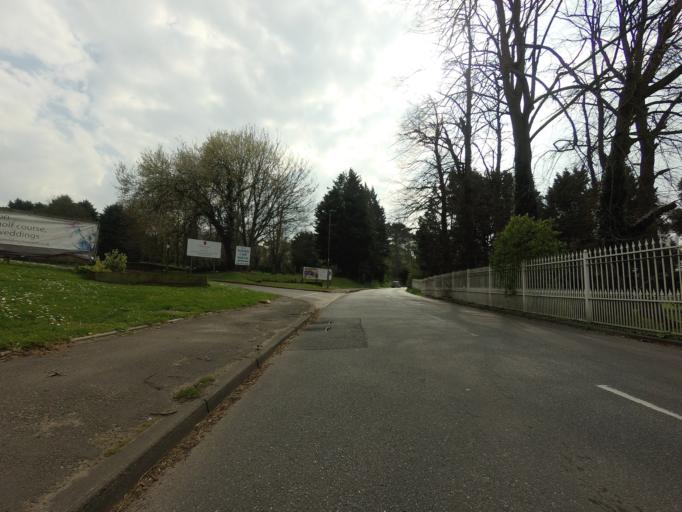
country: GB
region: England
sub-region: Greater London
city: Sidcup
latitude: 51.4053
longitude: 0.1210
